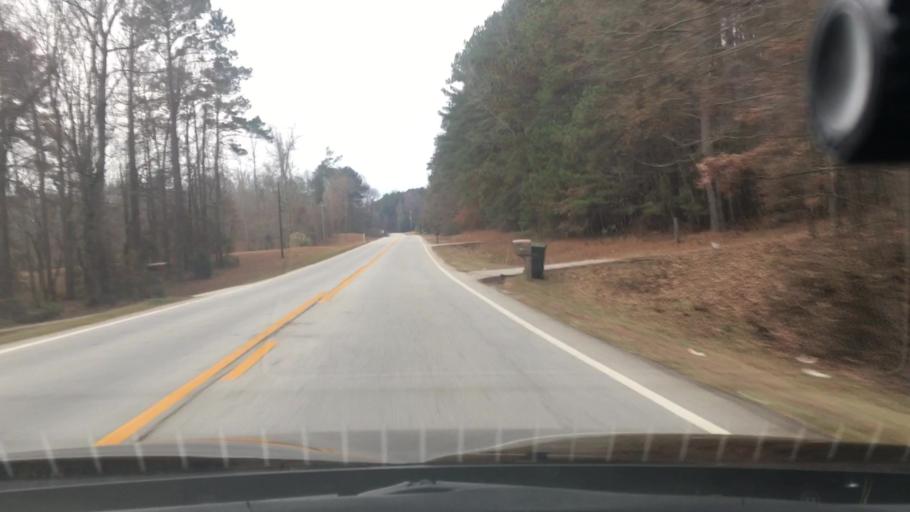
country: US
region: Georgia
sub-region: Fayette County
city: Peachtree City
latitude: 33.3533
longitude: -84.6379
